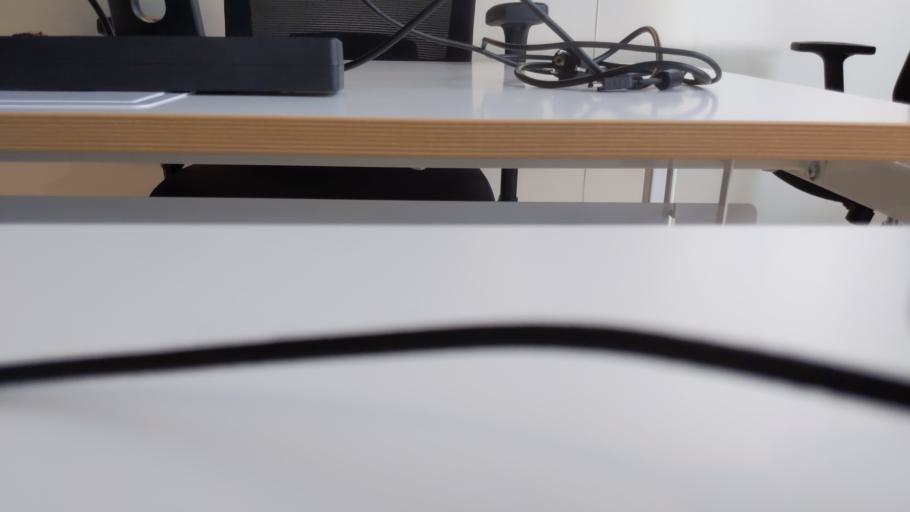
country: RU
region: Moskovskaya
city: Shevlyakovo
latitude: 56.4206
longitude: 37.0107
